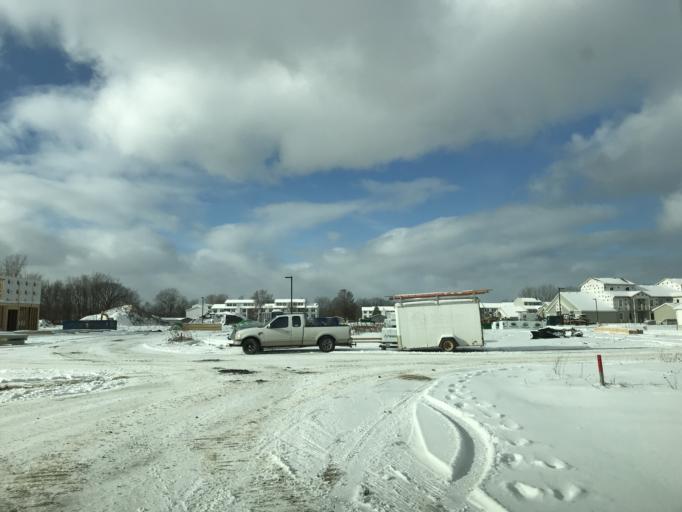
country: US
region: Michigan
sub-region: Kent County
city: Kentwood
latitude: 42.8509
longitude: -85.6451
